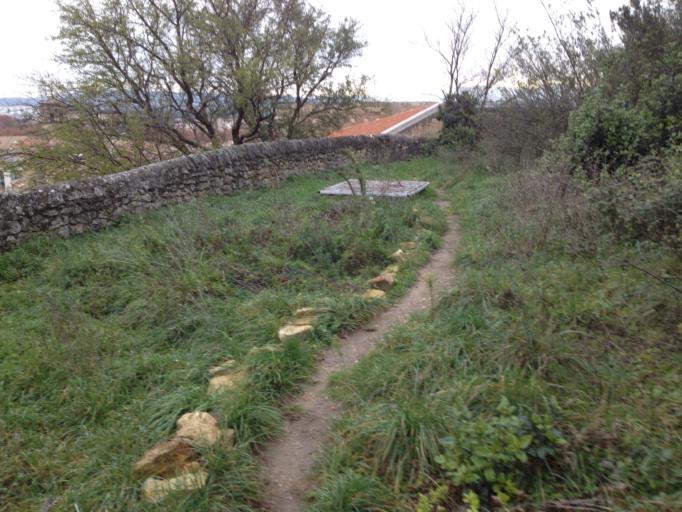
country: FR
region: Provence-Alpes-Cote d'Azur
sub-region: Departement du Vaucluse
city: Orange
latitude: 44.1351
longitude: 4.8078
